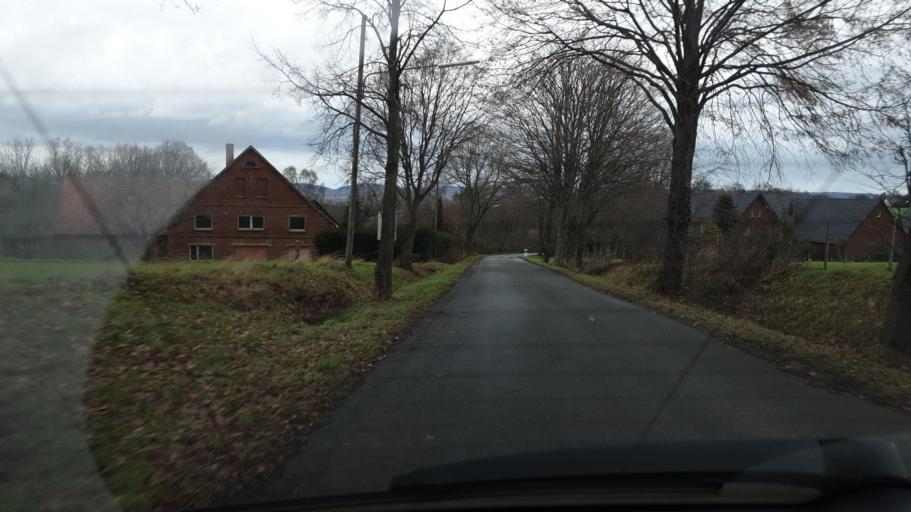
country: DE
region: North Rhine-Westphalia
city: Bad Oeynhausen
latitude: 52.1738
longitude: 8.7855
